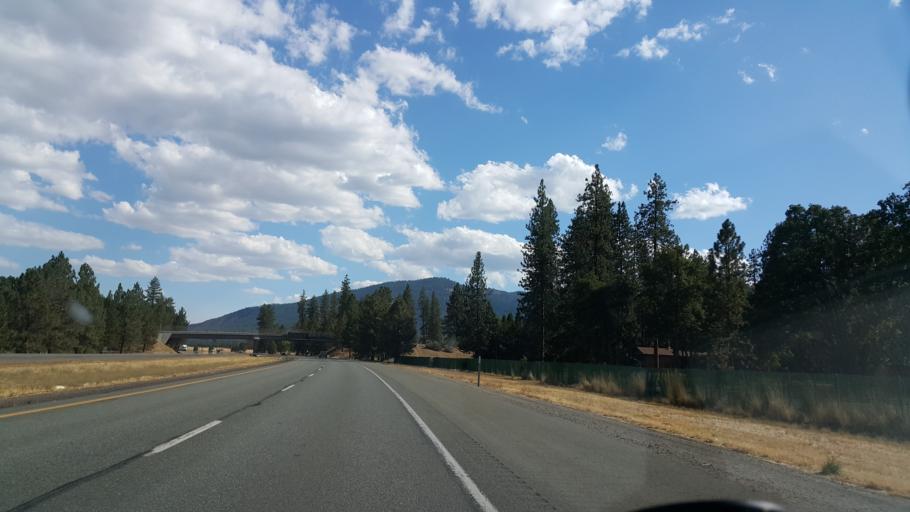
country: US
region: California
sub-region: Siskiyou County
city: Yreka
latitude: 41.6879
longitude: -122.6373
